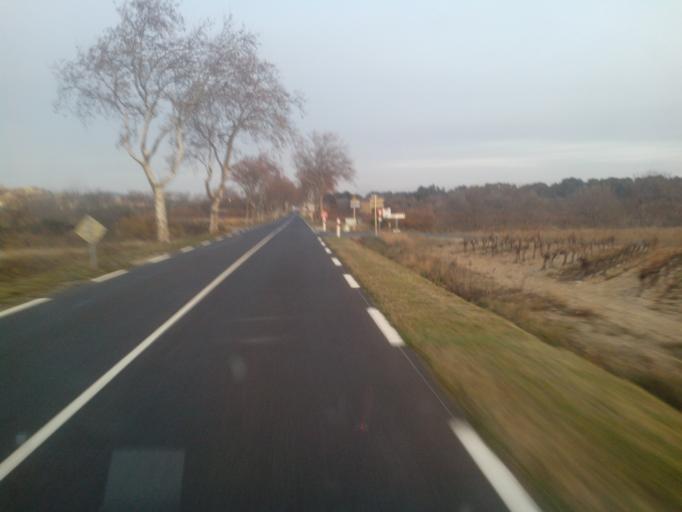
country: FR
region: Languedoc-Roussillon
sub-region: Departement de l'Aude
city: Ginestas
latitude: 43.2817
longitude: 2.8173
